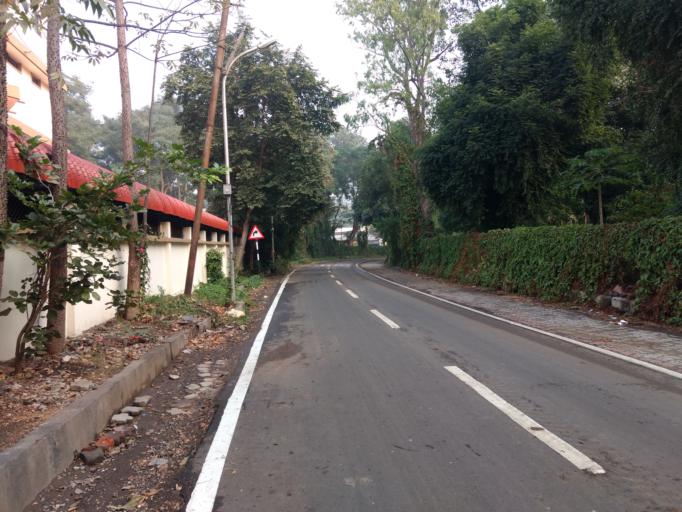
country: IN
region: Maharashtra
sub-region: Nagpur Division
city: Nagpur
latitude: 21.1558
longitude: 79.0502
